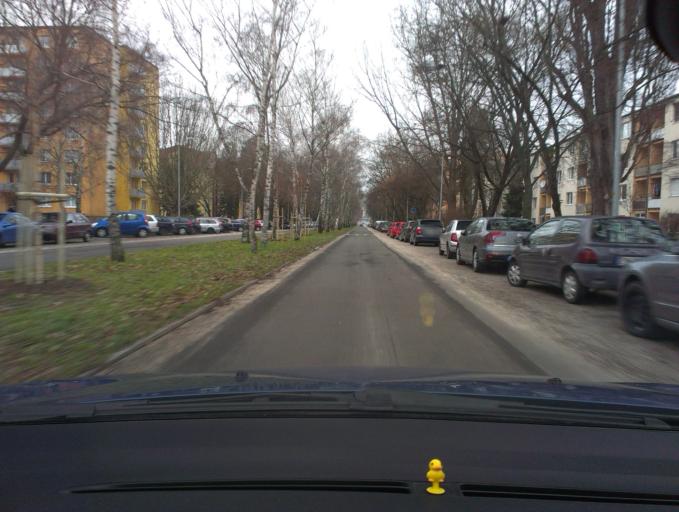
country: SK
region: Trnavsky
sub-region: Okres Trnava
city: Piestany
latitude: 48.5957
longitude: 17.8231
